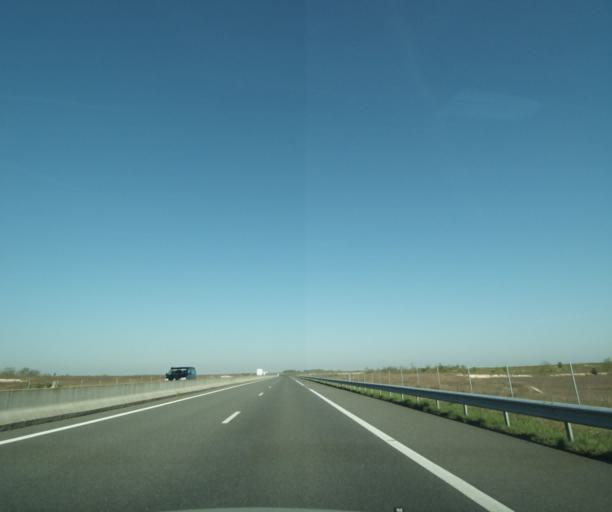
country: FR
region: Centre
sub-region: Departement du Loiret
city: Pannes
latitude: 48.0725
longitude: 2.6410
